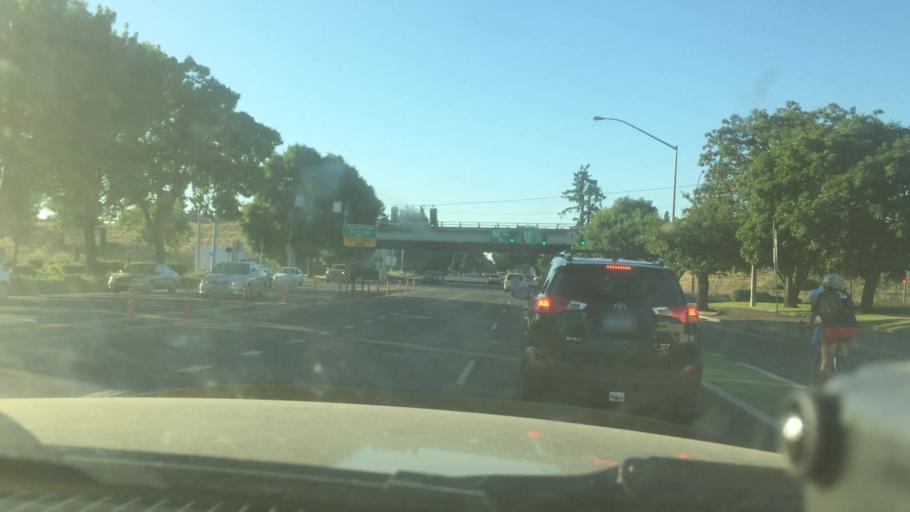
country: US
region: Oregon
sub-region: Lane County
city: Eugene
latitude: 44.0959
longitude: -123.1280
